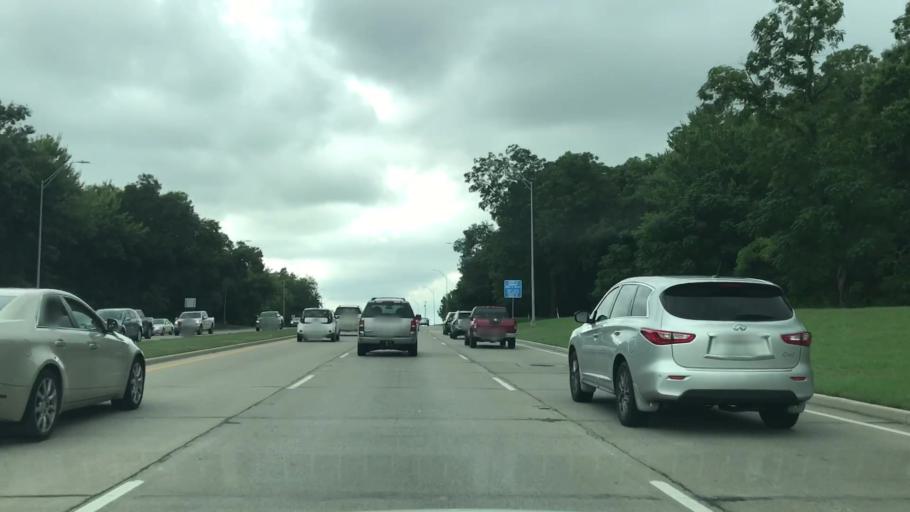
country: US
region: Texas
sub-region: Dallas County
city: Rowlett
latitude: 32.9104
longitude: -96.6000
